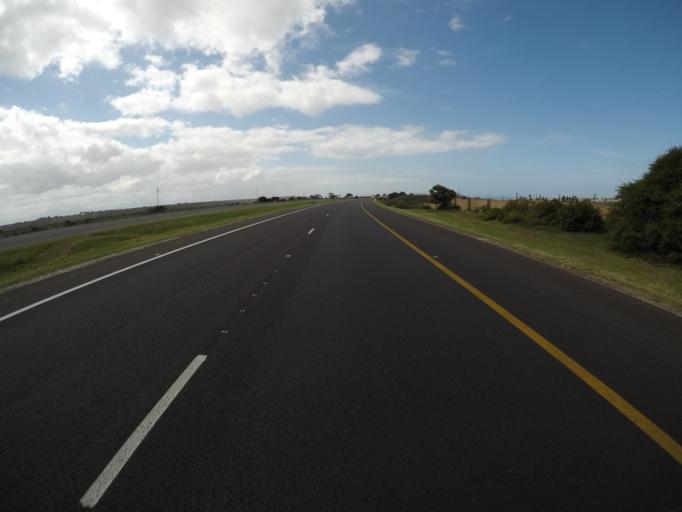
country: ZA
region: Western Cape
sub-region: Eden District Municipality
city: Mossel Bay
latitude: -34.1740
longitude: 22.0680
